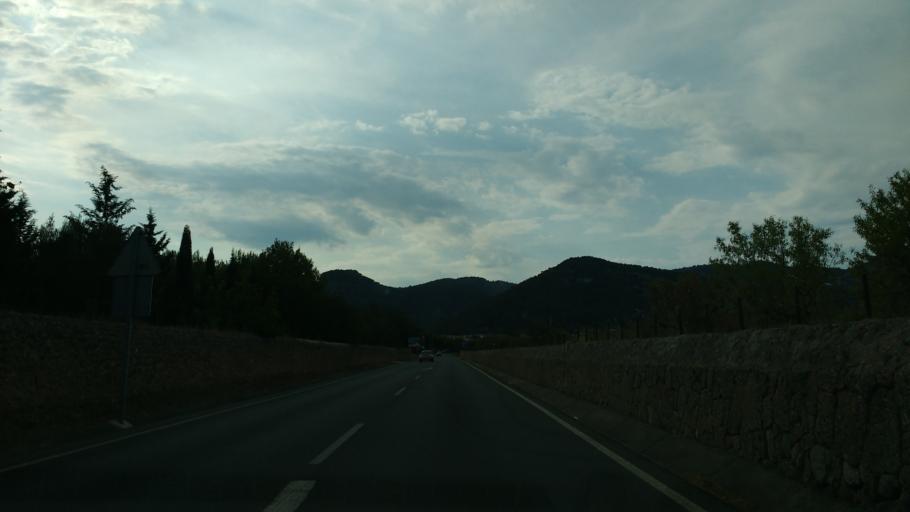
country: ES
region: Balearic Islands
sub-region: Illes Balears
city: Alaro
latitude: 39.6987
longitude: 2.7988
